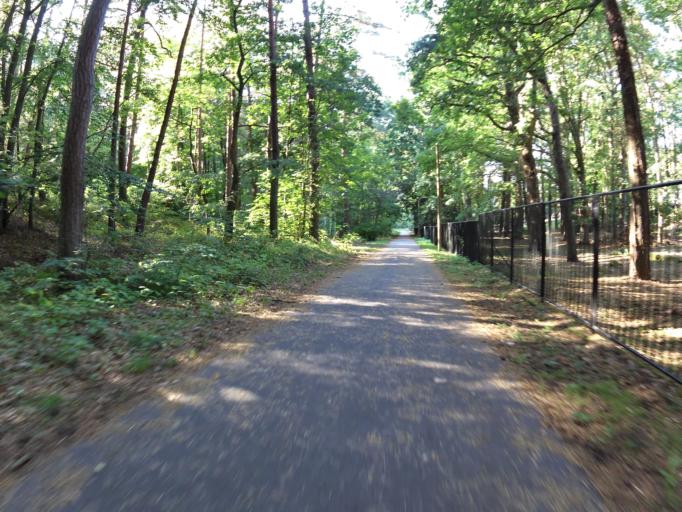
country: DE
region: Mecklenburg-Vorpommern
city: Seebad Heringsdorf
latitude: 53.9334
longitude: 14.2044
